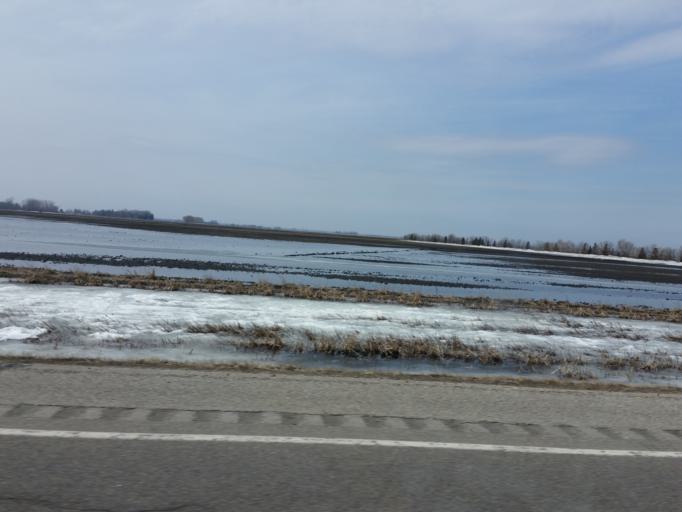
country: US
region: North Dakota
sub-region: Walsh County
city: Grafton
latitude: 48.3454
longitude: -97.4051
